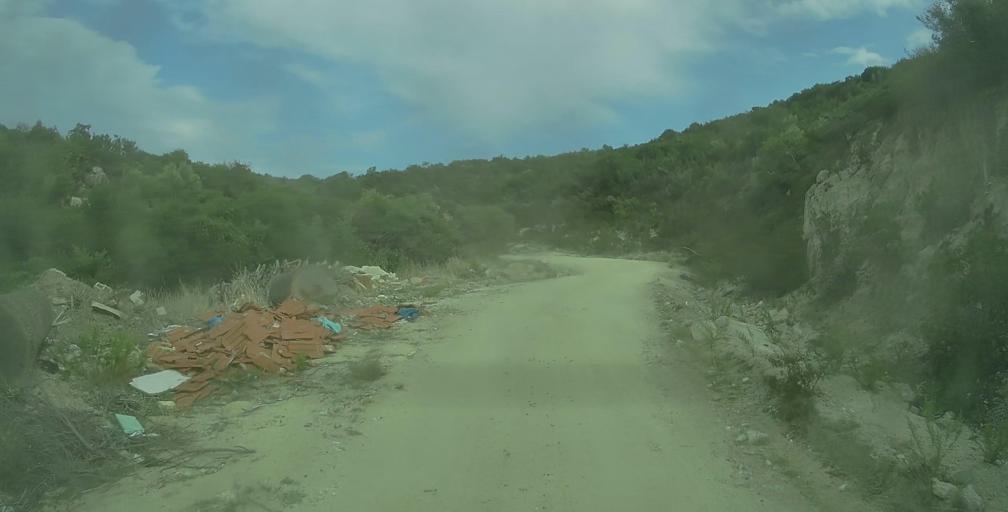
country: GR
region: Central Macedonia
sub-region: Nomos Chalkidikis
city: Sykia
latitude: 39.9896
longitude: 23.9163
